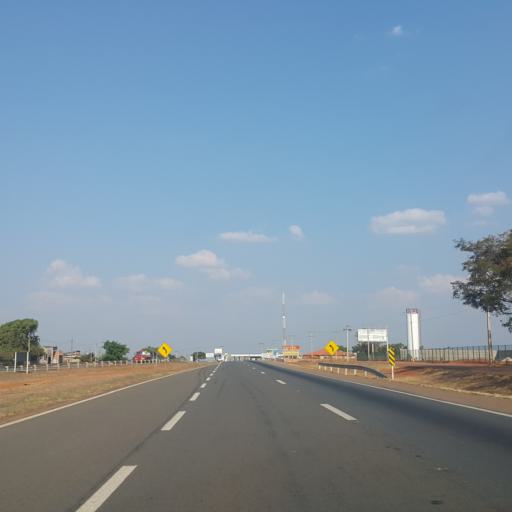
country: BR
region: Goias
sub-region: Abadiania
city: Abadiania
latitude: -16.1191
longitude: -48.4298
